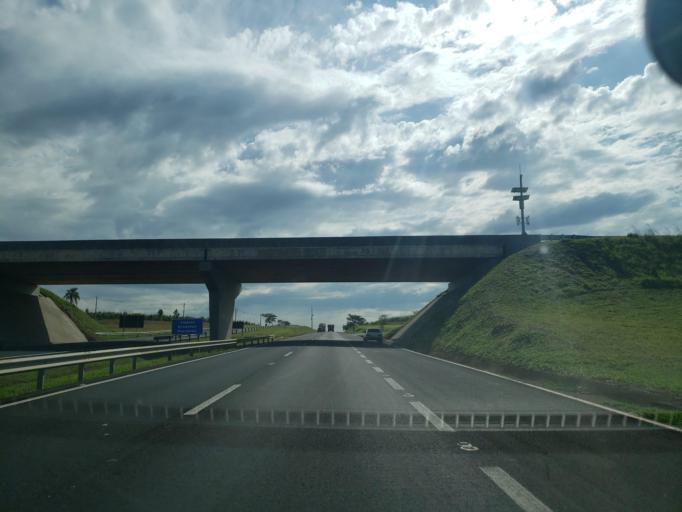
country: BR
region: Sao Paulo
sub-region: Cafelandia
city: Cafelandia
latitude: -21.8752
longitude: -49.5608
